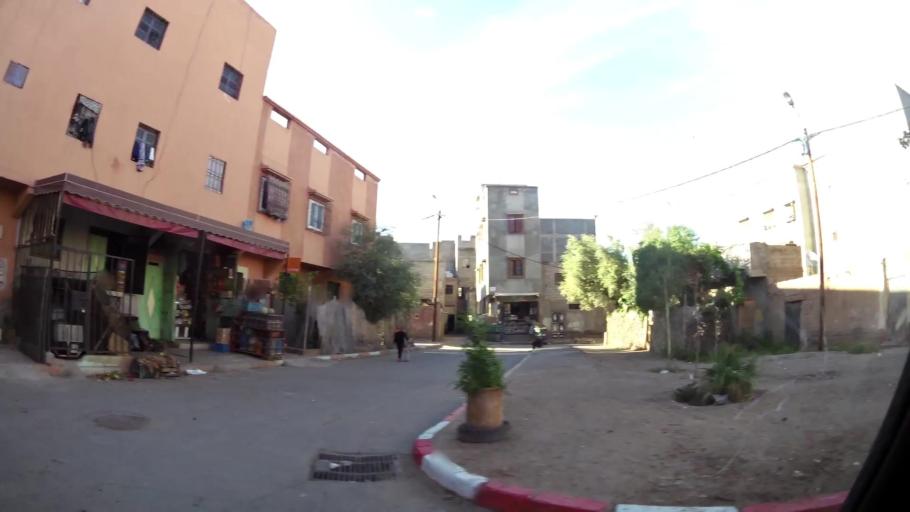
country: MA
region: Marrakech-Tensift-Al Haouz
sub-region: Marrakech
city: Marrakesh
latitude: 31.6168
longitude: -8.0689
